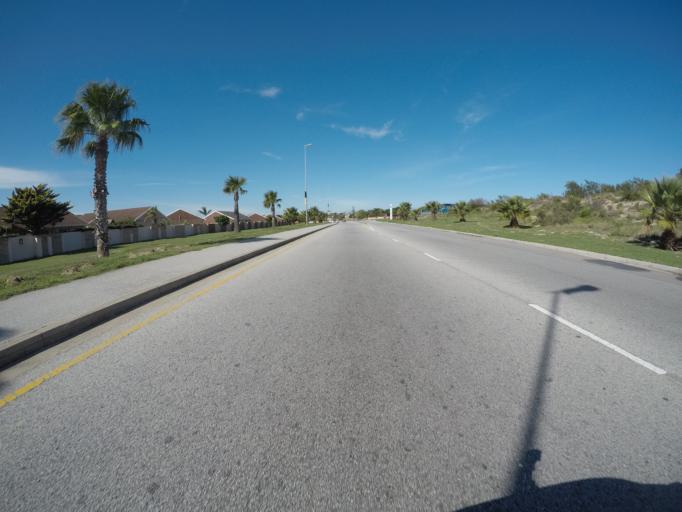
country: ZA
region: Eastern Cape
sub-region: Nelson Mandela Bay Metropolitan Municipality
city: Port Elizabeth
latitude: -33.9900
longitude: 25.6472
